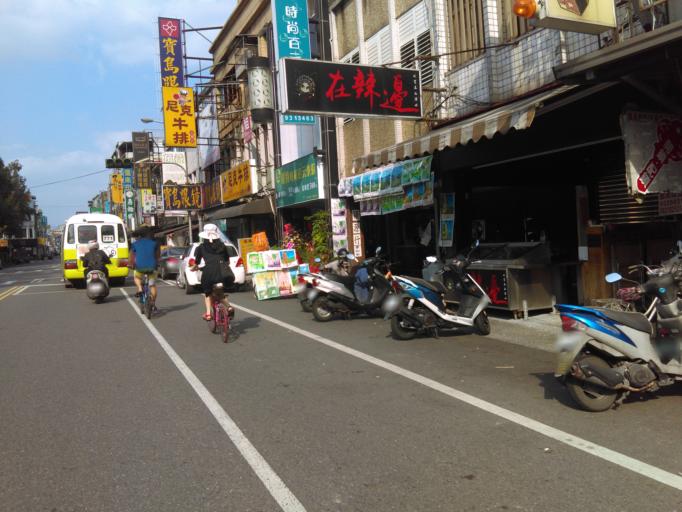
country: TW
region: Taiwan
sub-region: Yilan
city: Yilan
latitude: 24.7459
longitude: 121.7489
